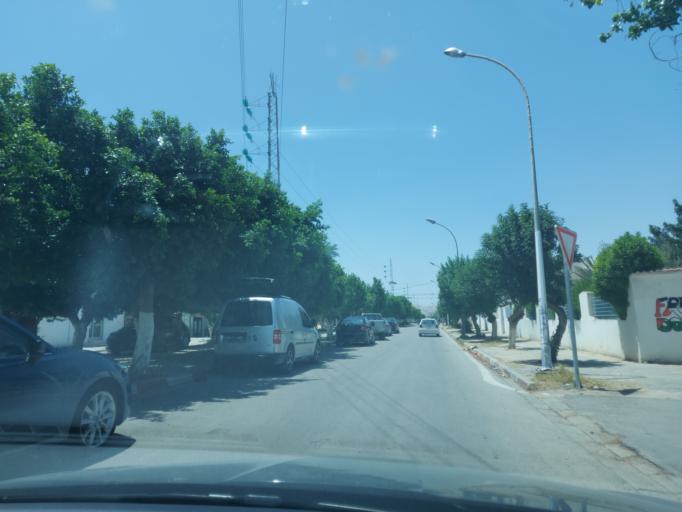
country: TN
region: Silyanah
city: Siliana
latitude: 36.0847
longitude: 9.3729
